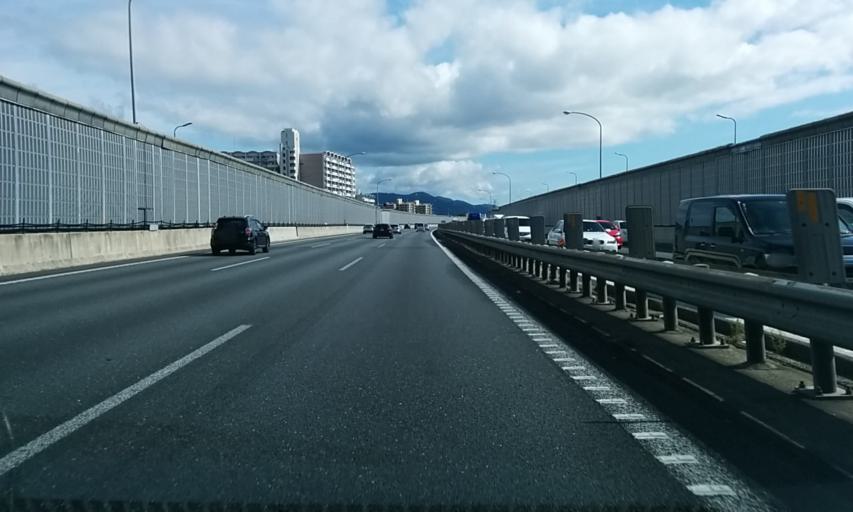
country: JP
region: Hyogo
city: Takarazuka
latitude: 34.8077
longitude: 135.3818
